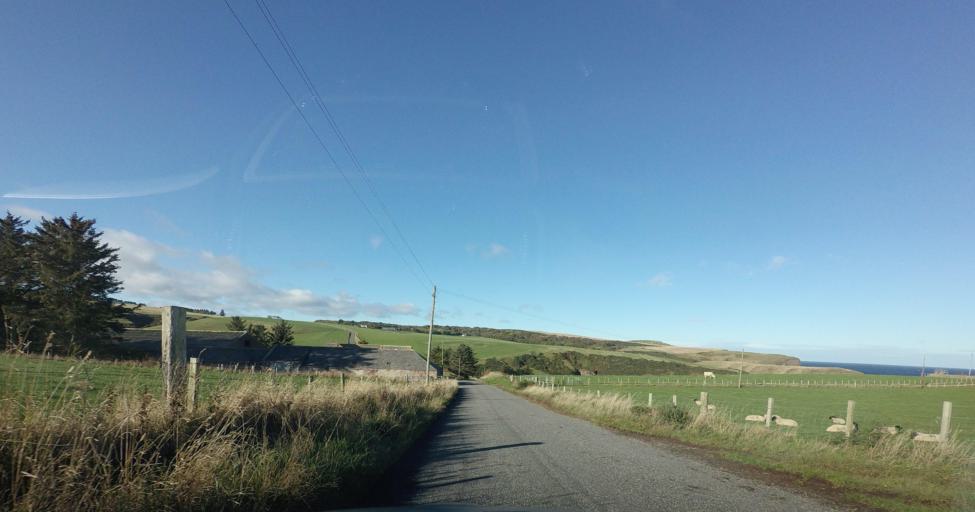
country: GB
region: Scotland
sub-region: Aberdeenshire
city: Rosehearty
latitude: 57.6793
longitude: -2.2660
